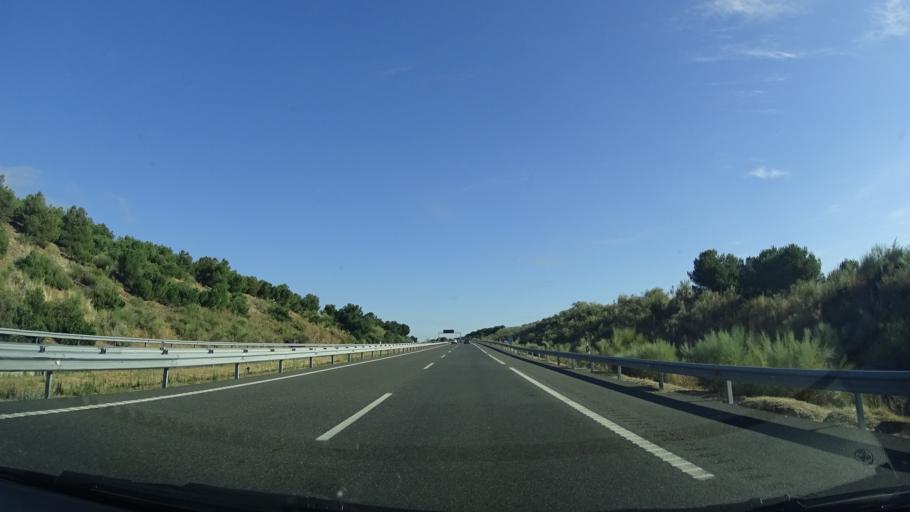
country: ES
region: Castille and Leon
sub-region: Provincia de Avila
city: Sanchidrian
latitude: 40.8720
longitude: -4.5669
